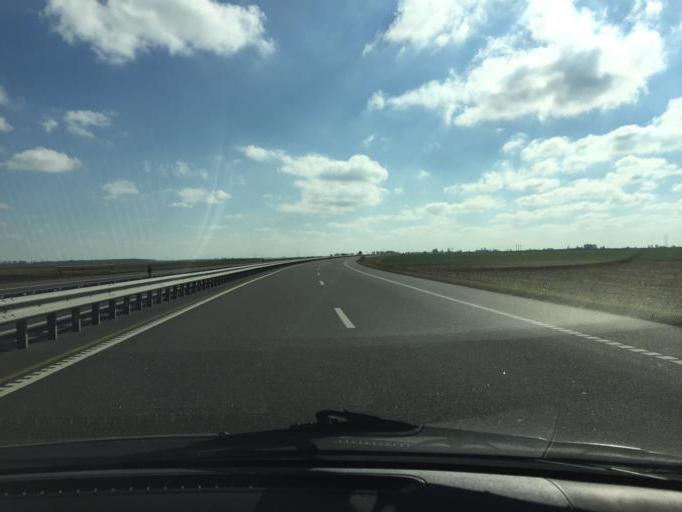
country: BY
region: Minsk
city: Slutsk
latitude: 53.1322
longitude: 27.5582
